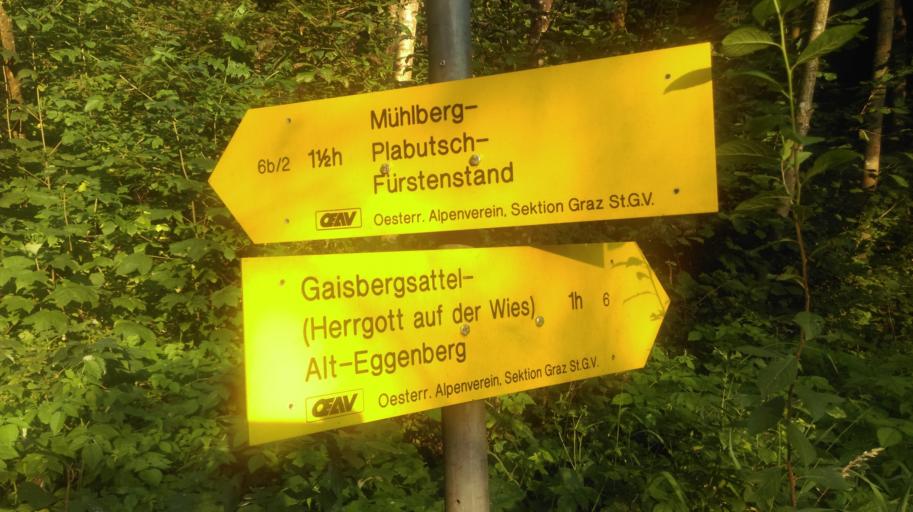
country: AT
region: Styria
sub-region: Politischer Bezirk Graz-Umgebung
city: Thal
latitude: 47.0702
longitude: 15.3685
